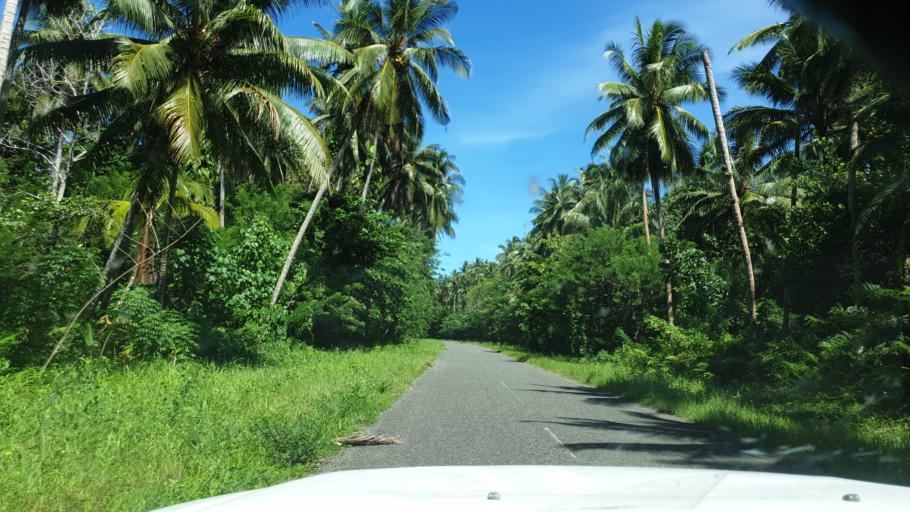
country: PG
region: Madang
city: Madang
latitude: -4.4681
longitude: 145.4158
